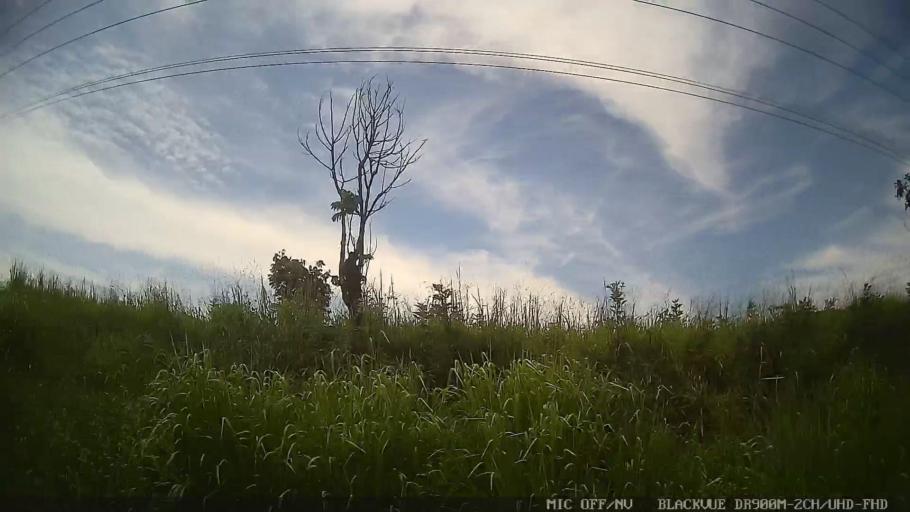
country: BR
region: Sao Paulo
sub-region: Aruja
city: Aruja
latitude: -23.4301
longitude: -46.2467
